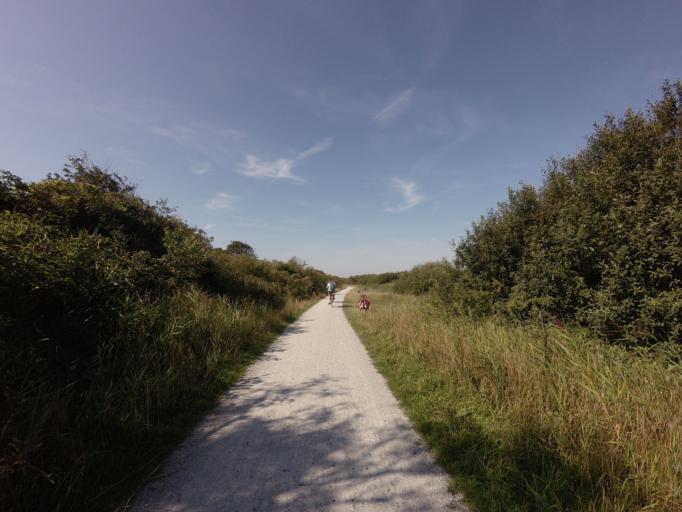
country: NL
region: Friesland
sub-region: Gemeente Schiermonnikoog
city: Schiermonnikoog
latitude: 53.4717
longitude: 6.1538
